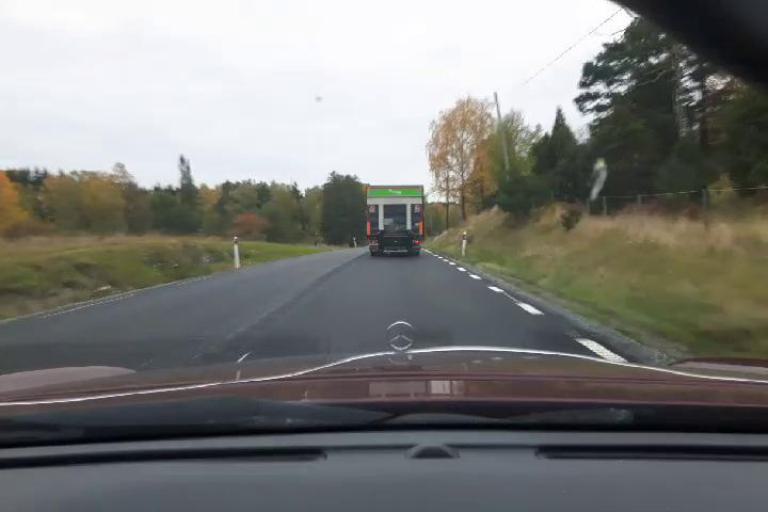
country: SE
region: Soedermanland
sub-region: Strangnas Kommun
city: Strangnas
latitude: 59.4327
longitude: 17.0234
